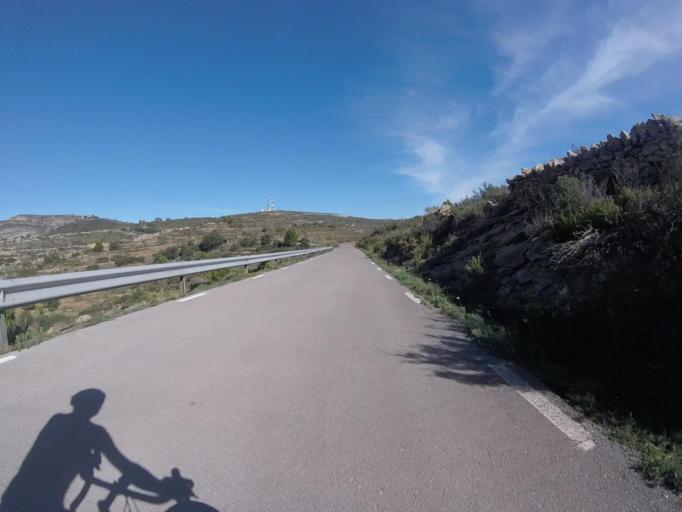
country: ES
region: Valencia
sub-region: Provincia de Castello
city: Sarratella
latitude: 40.2946
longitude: 0.0308
